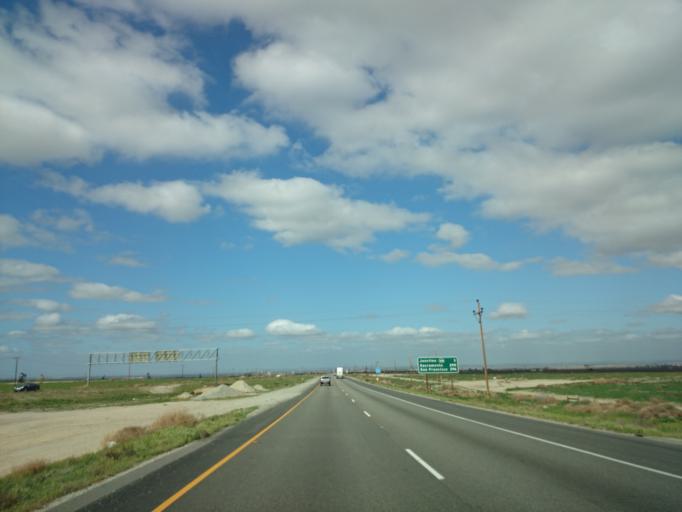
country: US
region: California
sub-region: Kern County
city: Frazier Park
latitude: 35.0209
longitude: -118.9584
